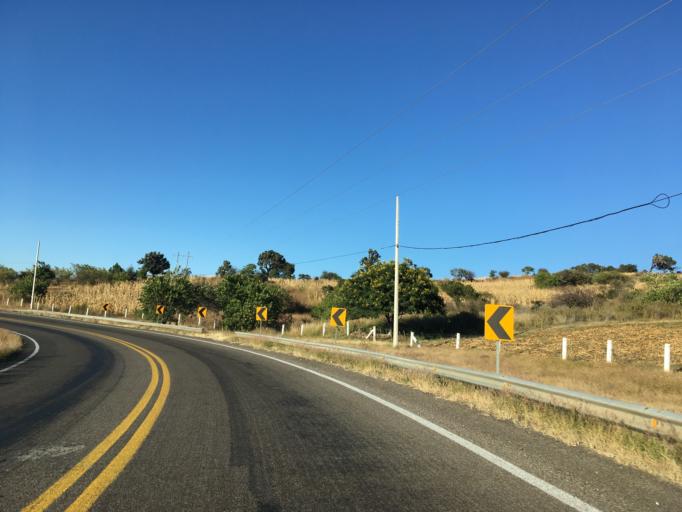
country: MX
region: Michoacan
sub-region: Tuxpan
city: La Soledad
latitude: 19.5195
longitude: -100.4717
